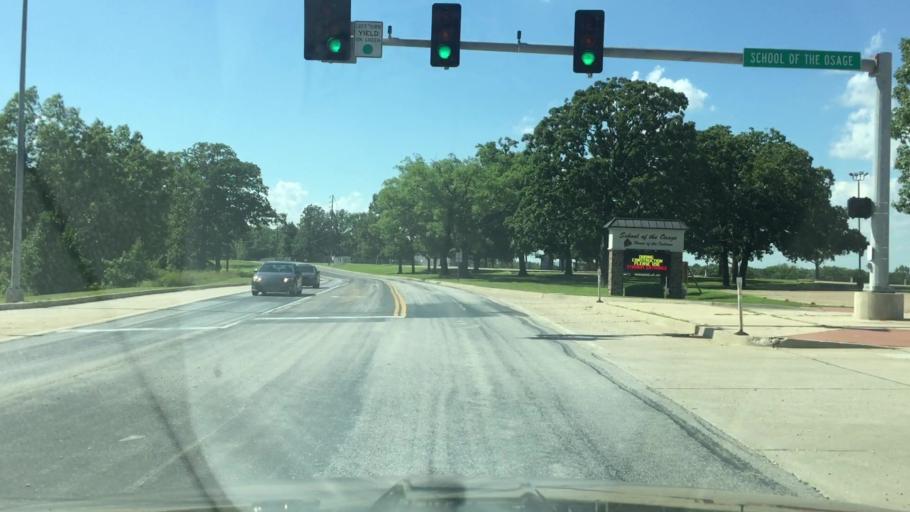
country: US
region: Missouri
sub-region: Camden County
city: Osage Beach
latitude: 38.1459
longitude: -92.5923
